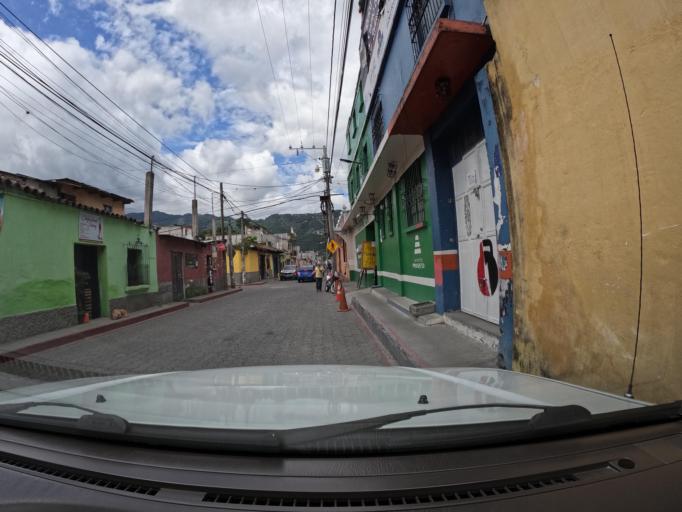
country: GT
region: Sacatepequez
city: Jocotenango
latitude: 14.5743
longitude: -90.7404
